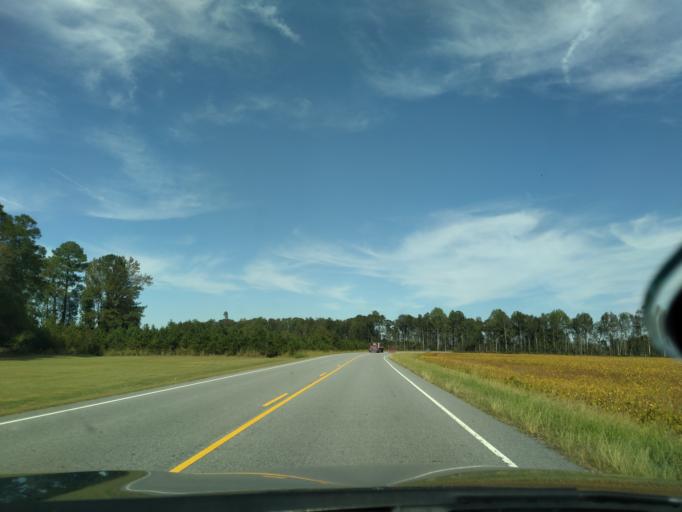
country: US
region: North Carolina
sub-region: Beaufort County
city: River Road
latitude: 35.5202
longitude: -76.8929
